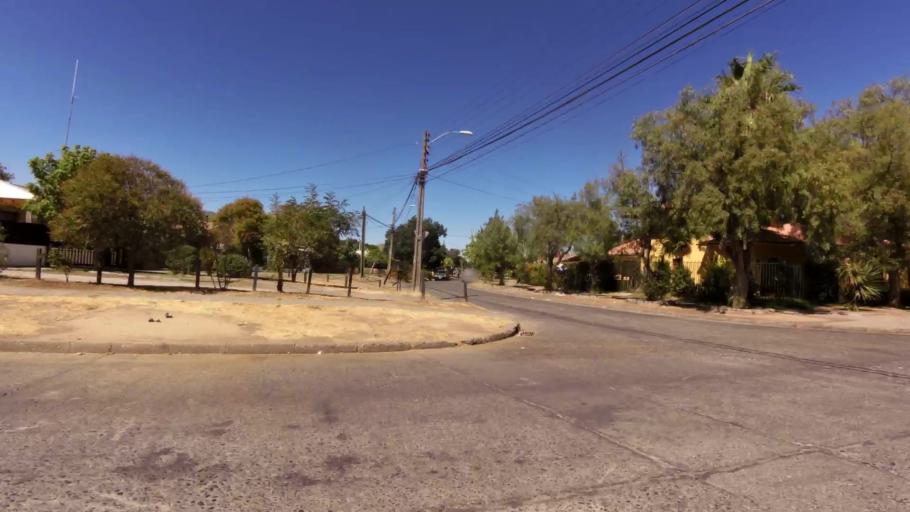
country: CL
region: O'Higgins
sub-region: Provincia de Cachapoal
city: Rancagua
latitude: -34.1772
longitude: -70.7174
